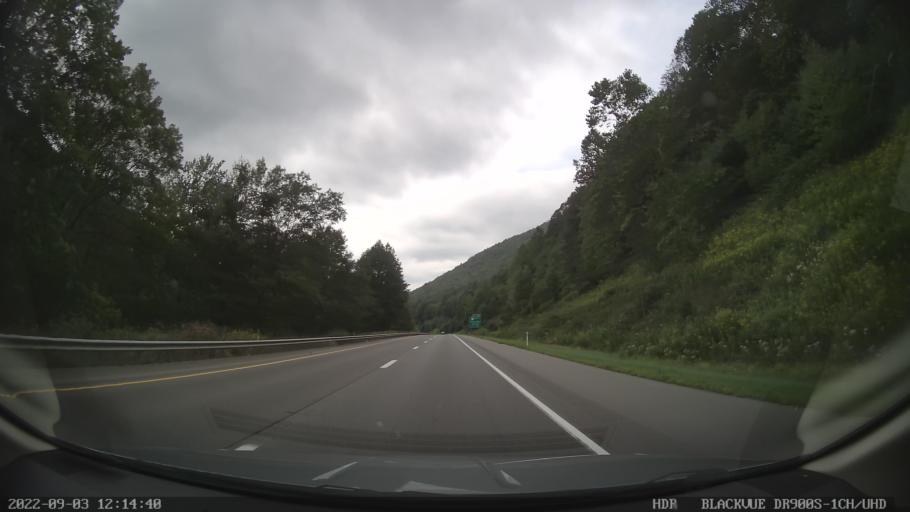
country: US
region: Pennsylvania
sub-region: Lycoming County
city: Garden View
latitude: 41.3975
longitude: -77.0648
